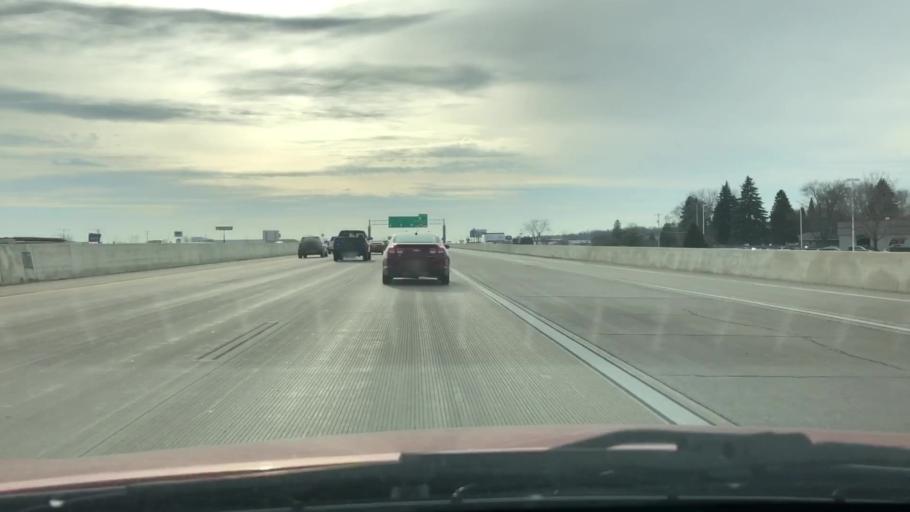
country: US
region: Wisconsin
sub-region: Brown County
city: De Pere
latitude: 44.4478
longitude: -88.0937
